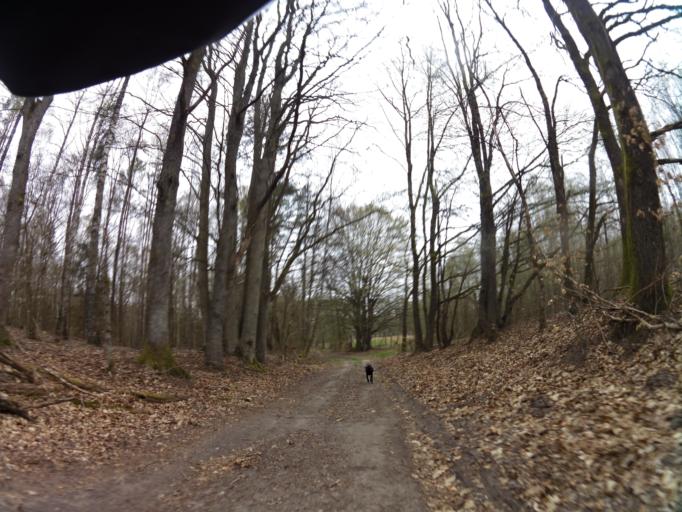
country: PL
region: West Pomeranian Voivodeship
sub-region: Powiat koszalinski
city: Bobolice
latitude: 53.9382
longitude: 16.6989
